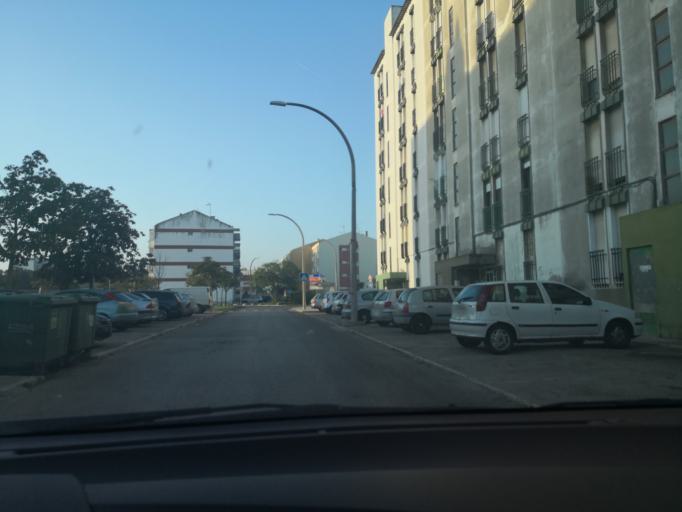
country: PT
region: Setubal
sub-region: Moita
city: Alhos Vedros
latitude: 38.6503
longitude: -9.0403
